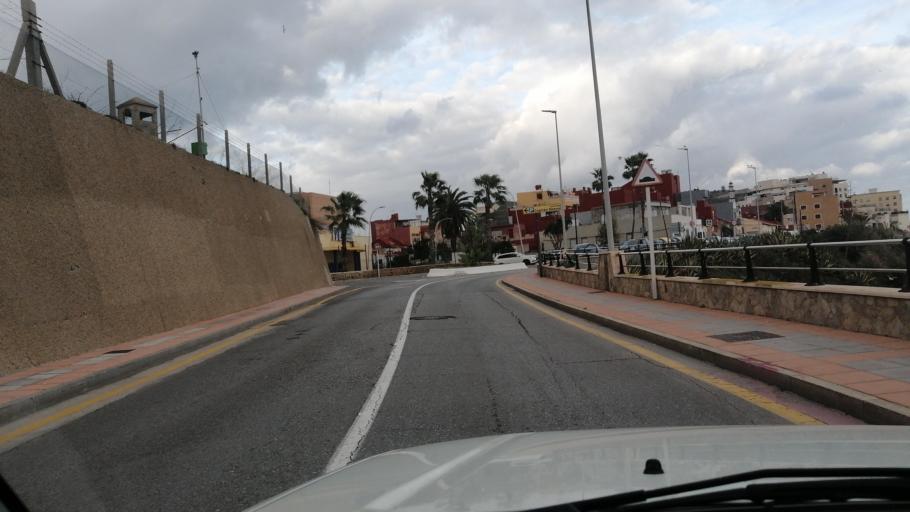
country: ES
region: Ceuta
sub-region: Ceuta
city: Ceuta
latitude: 35.8859
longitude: -5.3050
